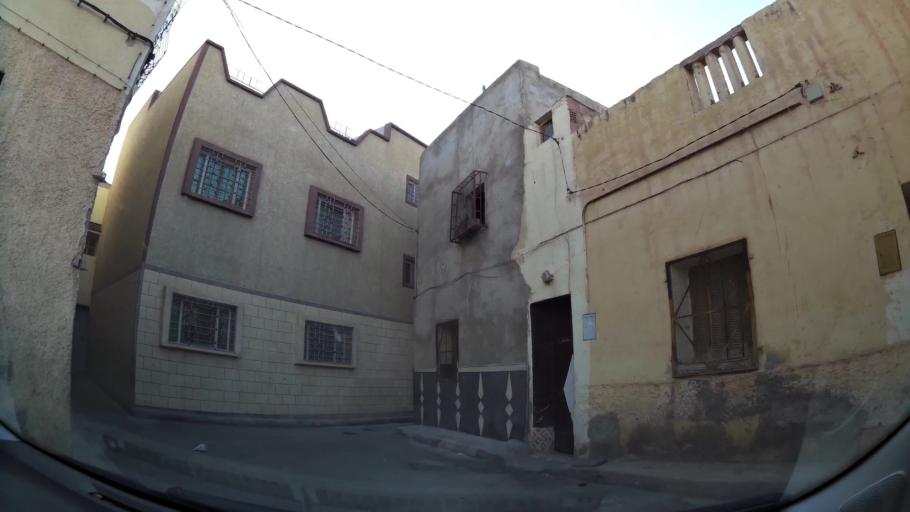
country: MA
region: Oriental
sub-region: Oujda-Angad
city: Oujda
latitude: 34.7003
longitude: -1.9076
